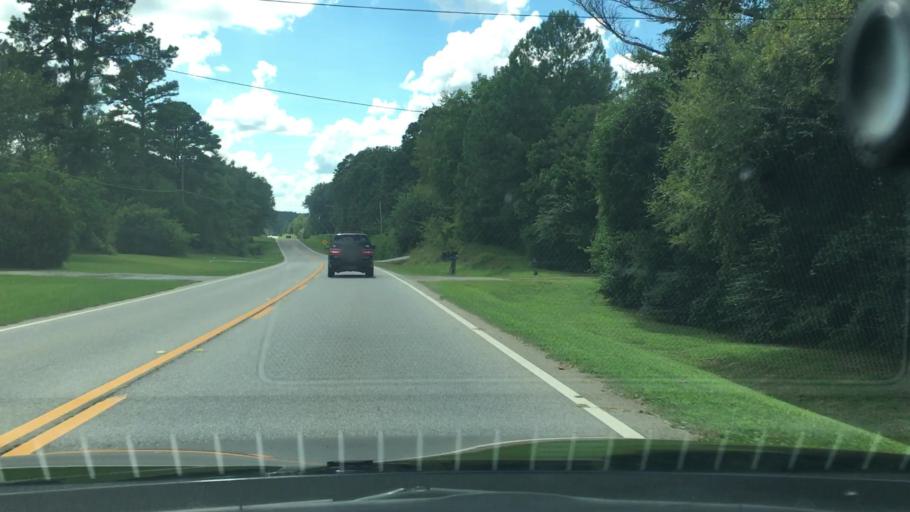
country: US
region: Georgia
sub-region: Putnam County
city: Eatonton
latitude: 33.3179
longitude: -83.4209
